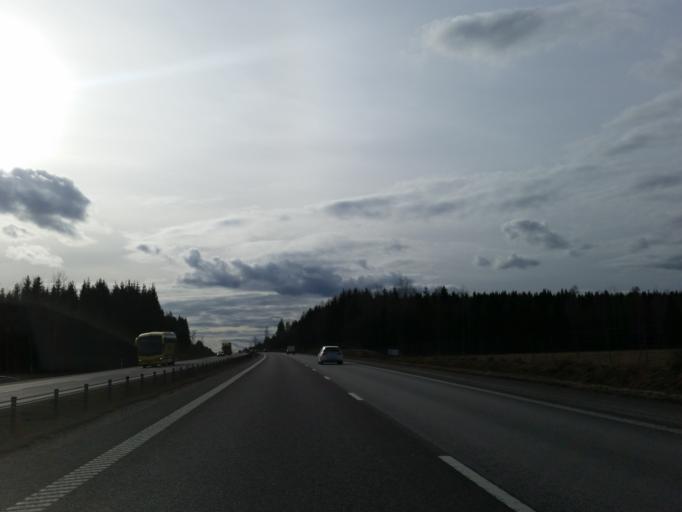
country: SE
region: OEstergoetland
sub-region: Norrkopings Kommun
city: Krokek
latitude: 58.7421
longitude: 16.4630
